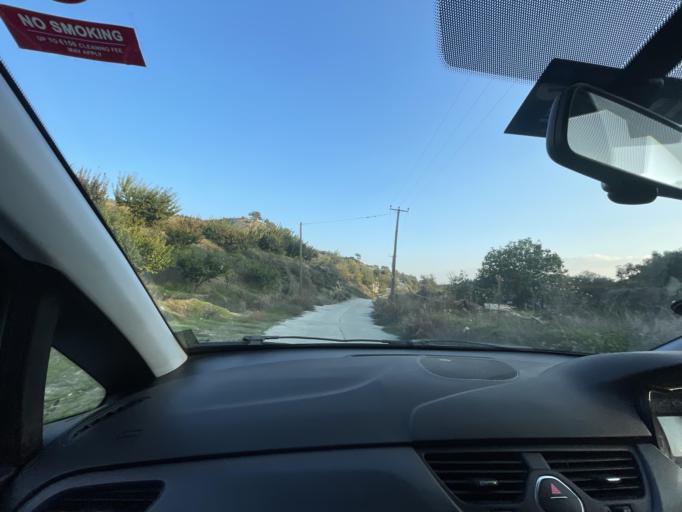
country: CY
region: Limassol
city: Pelendri
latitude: 34.8899
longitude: 32.9710
